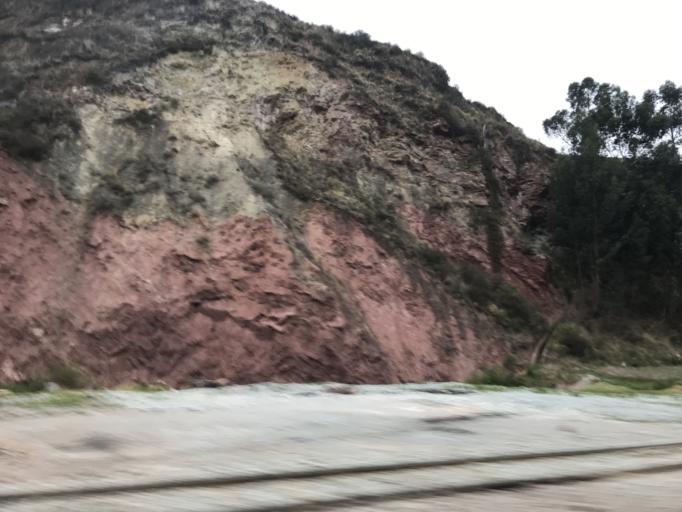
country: PE
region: Cusco
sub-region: Provincia de Anta
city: Huarocondo
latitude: -13.3972
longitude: -72.2114
